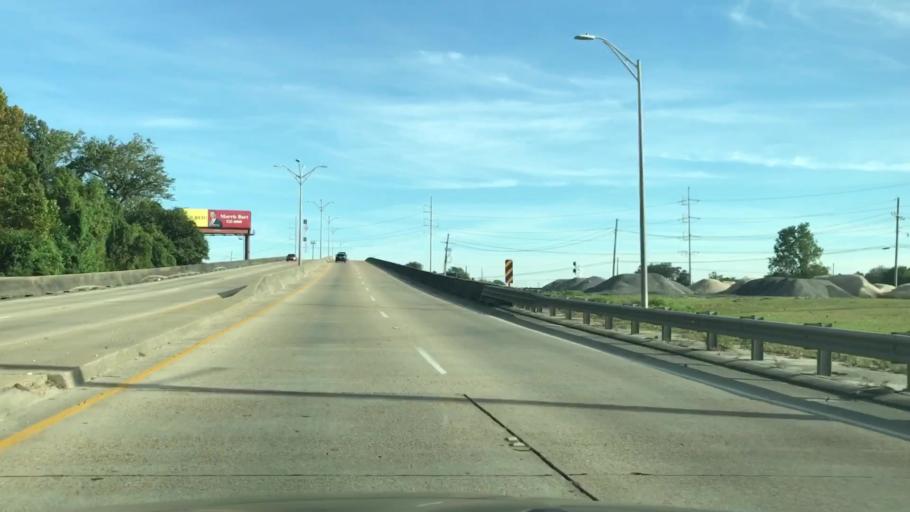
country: US
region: Louisiana
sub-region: Jefferson Parish
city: River Ridge
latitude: 29.9750
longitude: -90.2085
